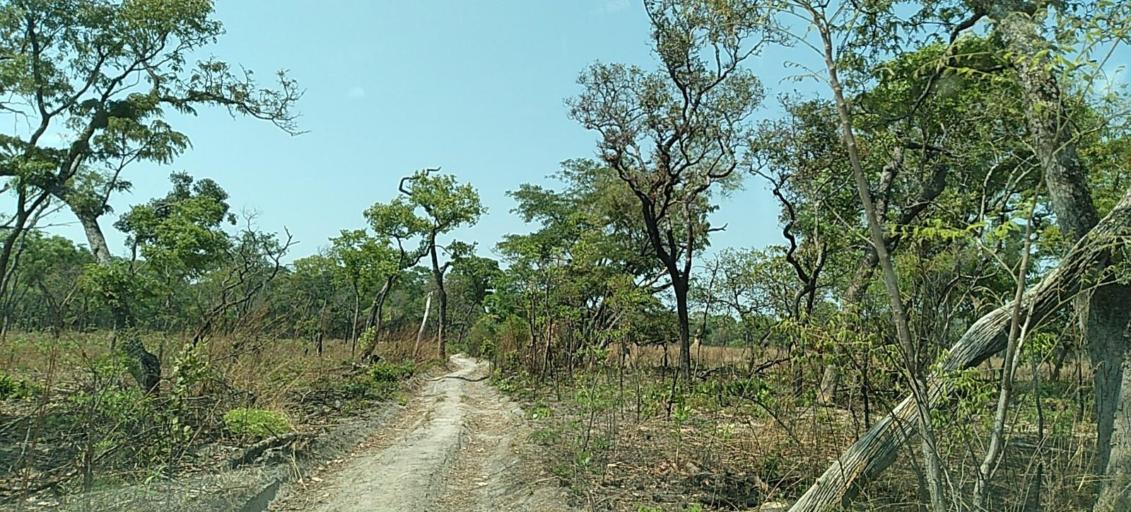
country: ZM
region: Copperbelt
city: Mpongwe
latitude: -13.7858
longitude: 28.0989
